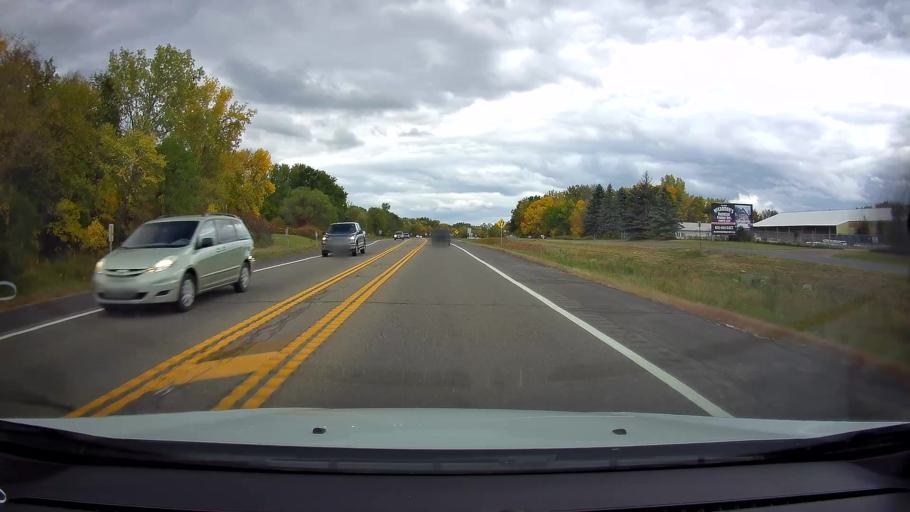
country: US
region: Minnesota
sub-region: Washington County
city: Forest Lake
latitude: 45.2957
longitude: -92.9746
